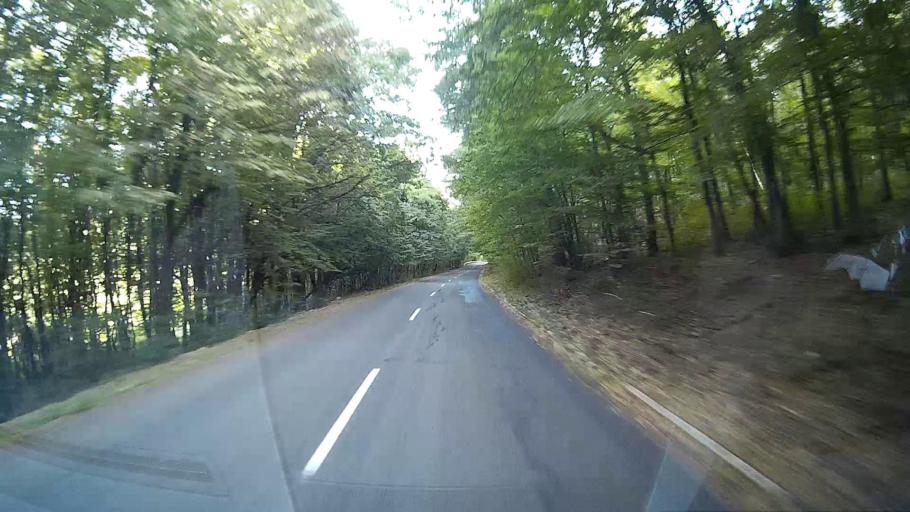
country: HU
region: Pest
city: Visegrad
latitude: 47.7234
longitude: 18.9816
